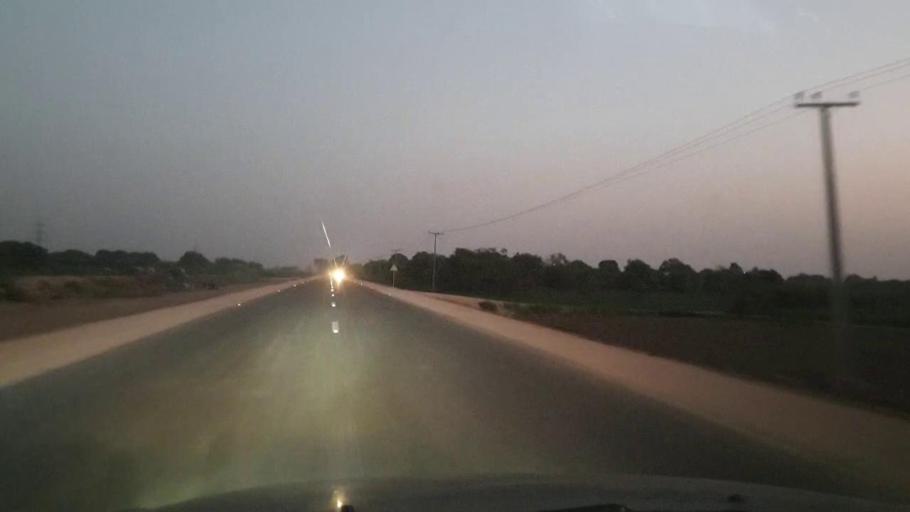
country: PK
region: Sindh
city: Tando Allahyar
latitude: 25.3926
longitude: 68.7679
